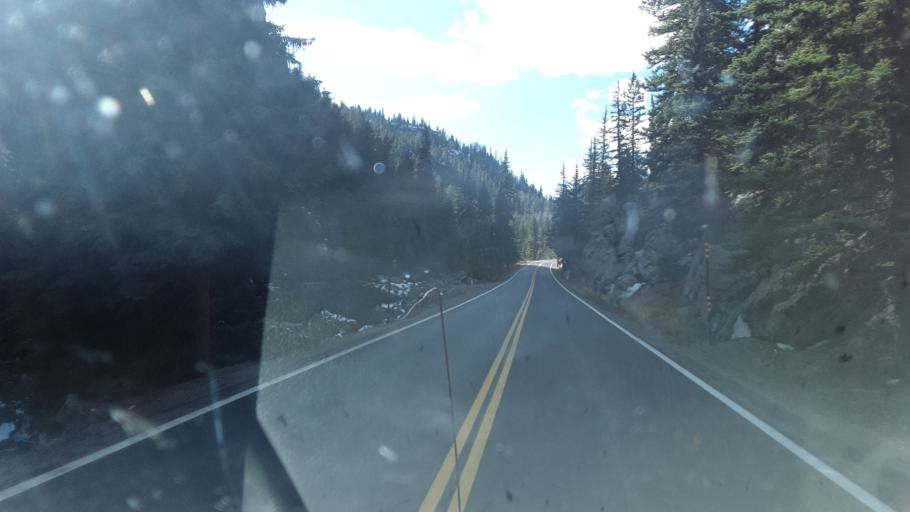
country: US
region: Colorado
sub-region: Mineral County
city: Creede
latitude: 37.5688
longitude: -106.7610
